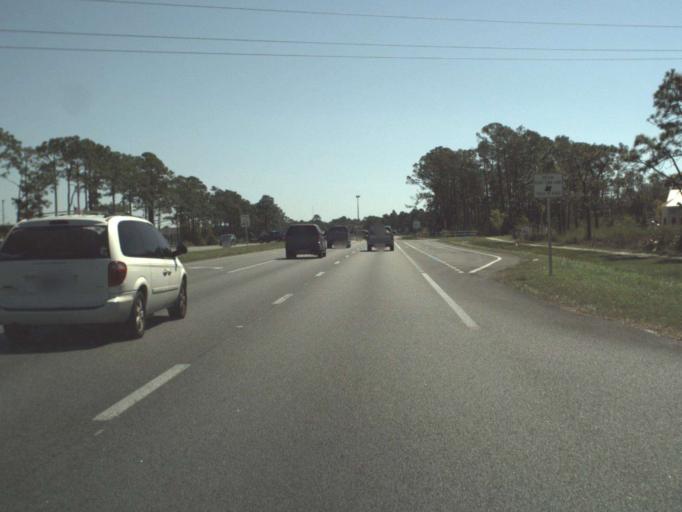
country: US
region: Florida
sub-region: Bay County
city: Panama City Beach
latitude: 30.1995
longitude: -85.8180
